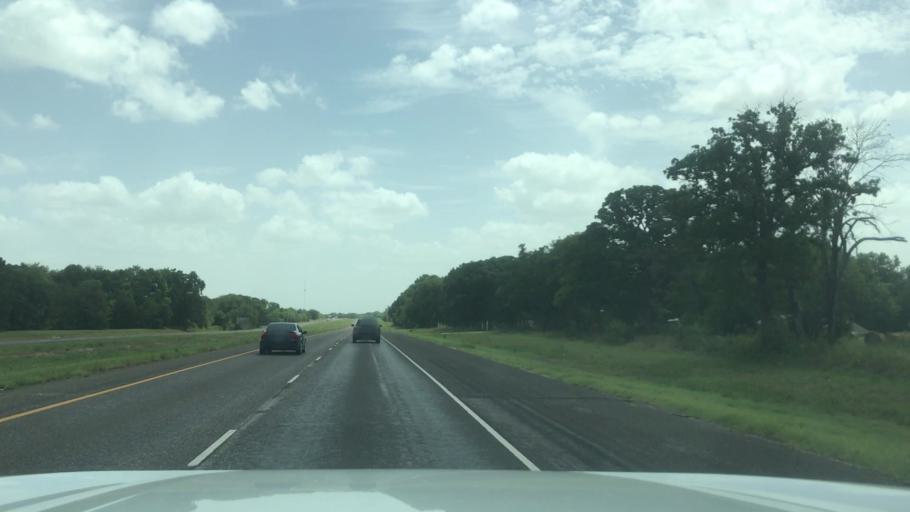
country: US
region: Texas
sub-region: Falls County
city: Marlin
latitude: 31.2931
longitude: -96.8751
